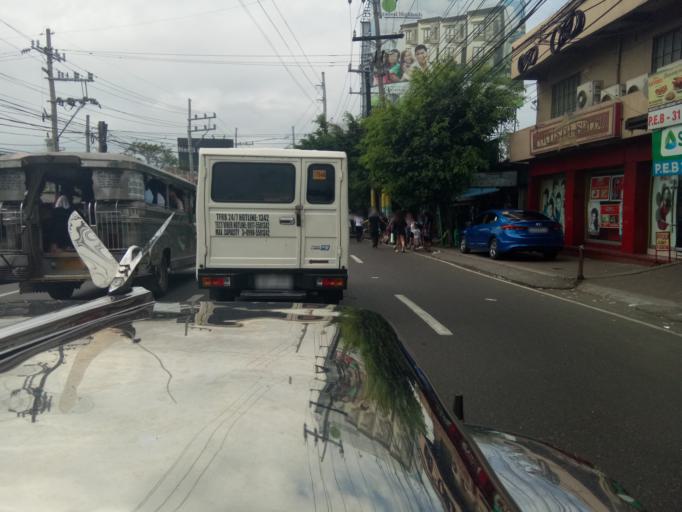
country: PH
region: Calabarzon
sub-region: Province of Cavite
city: Dasmarinas
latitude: 14.3026
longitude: 120.9540
